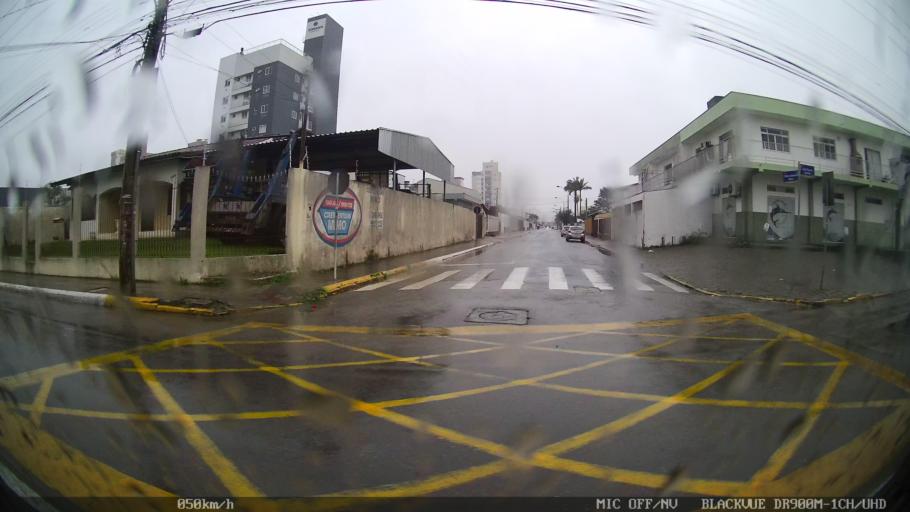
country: BR
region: Santa Catarina
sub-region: Itajai
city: Itajai
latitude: -26.9126
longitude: -48.6824
